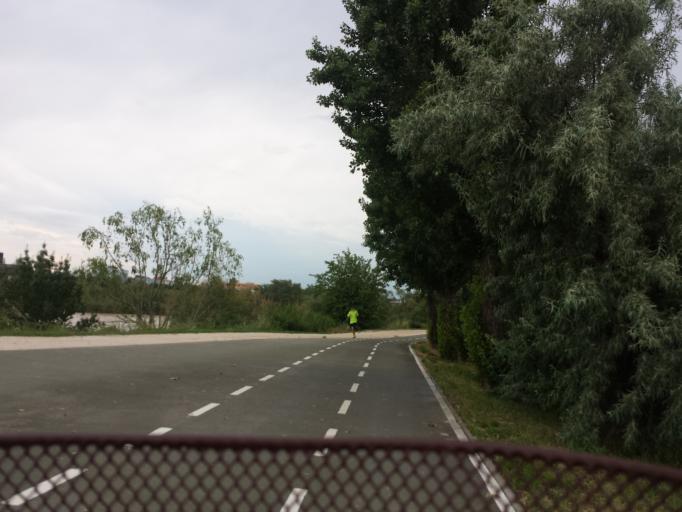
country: ES
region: Aragon
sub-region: Provincia de Zaragoza
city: Almozara
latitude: 41.6794
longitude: -0.9022
